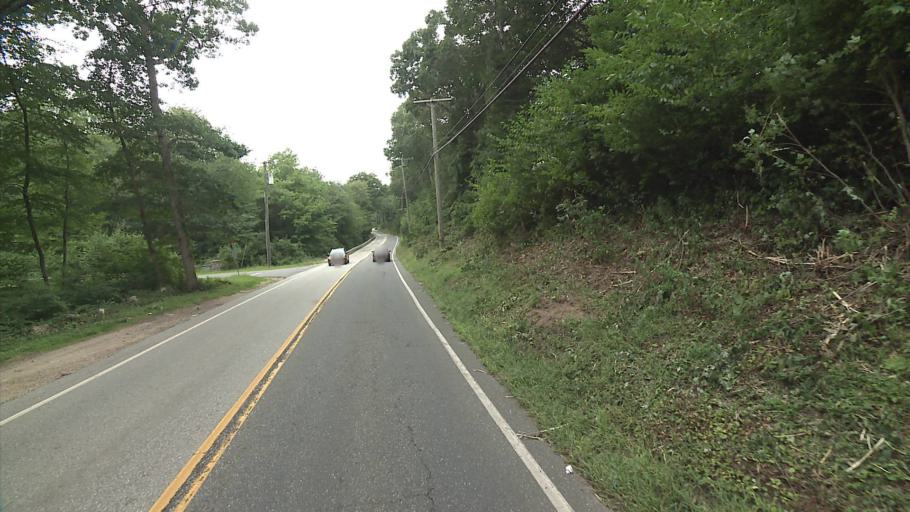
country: US
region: Connecticut
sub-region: New London County
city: Niantic
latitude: 41.3019
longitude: -72.2579
